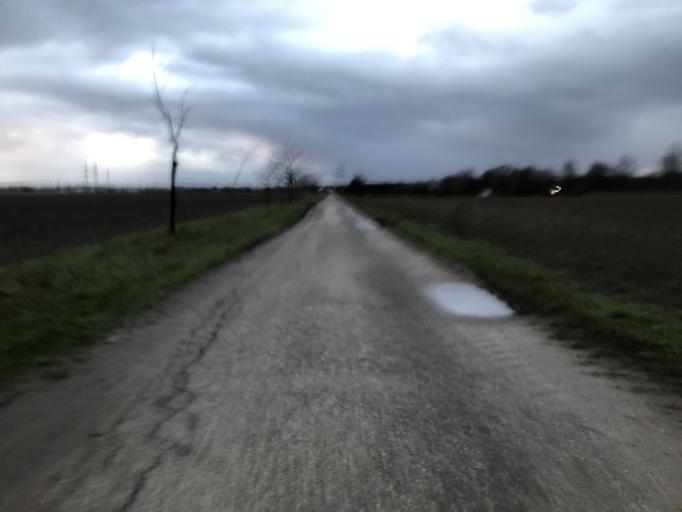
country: DE
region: Baden-Wuerttemberg
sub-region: Karlsruhe Region
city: Neulussheim
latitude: 49.3047
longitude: 8.5241
